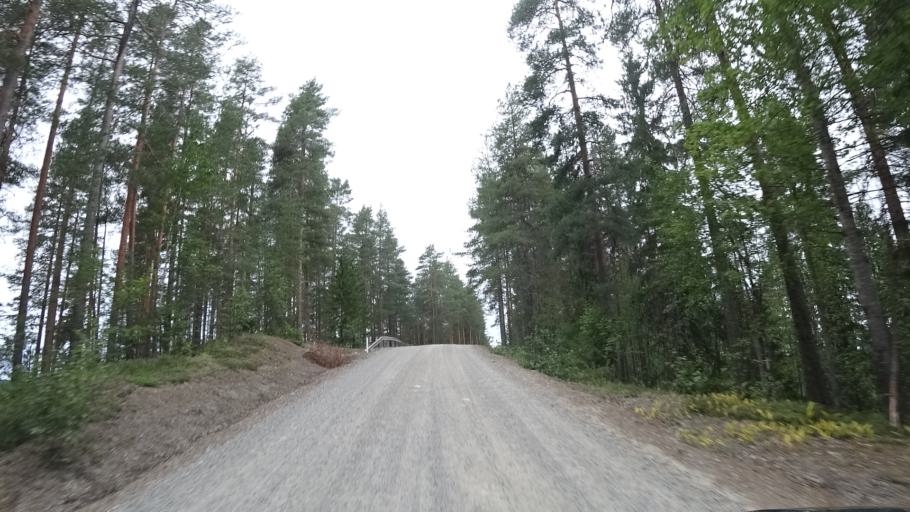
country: FI
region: North Karelia
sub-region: Pielisen Karjala
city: Lieksa
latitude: 63.2328
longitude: 30.3688
